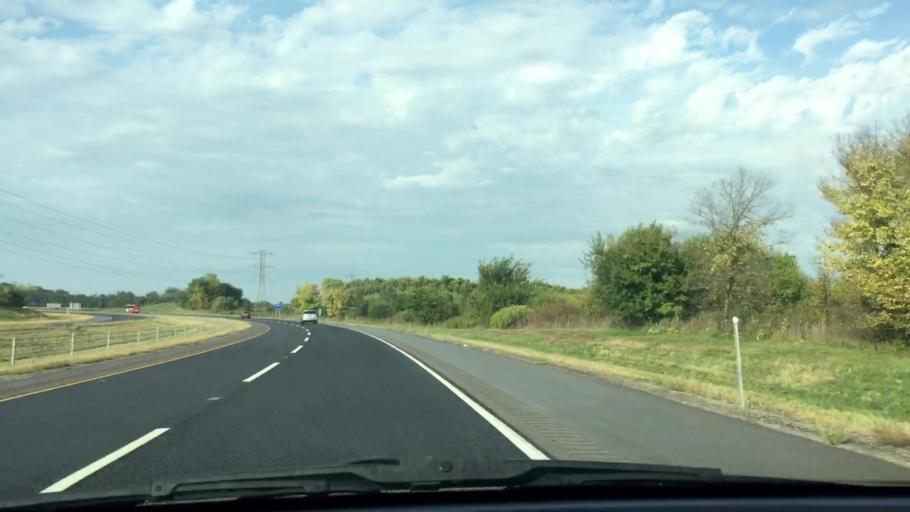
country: US
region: Illinois
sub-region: Whiteside County
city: Rock Falls
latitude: 41.7666
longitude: -89.6240
